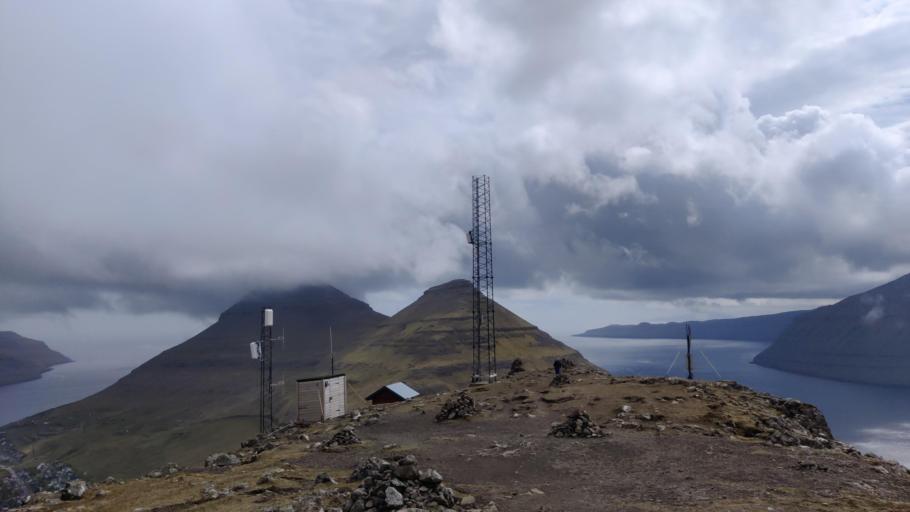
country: FO
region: Nordoyar
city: Klaksvik
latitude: 62.2351
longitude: -6.6166
